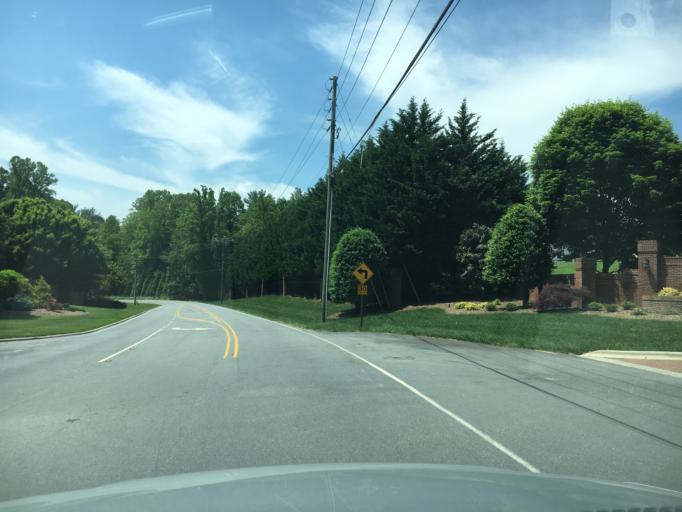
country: US
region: North Carolina
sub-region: Henderson County
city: Mountain Home
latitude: 35.3742
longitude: -82.5253
